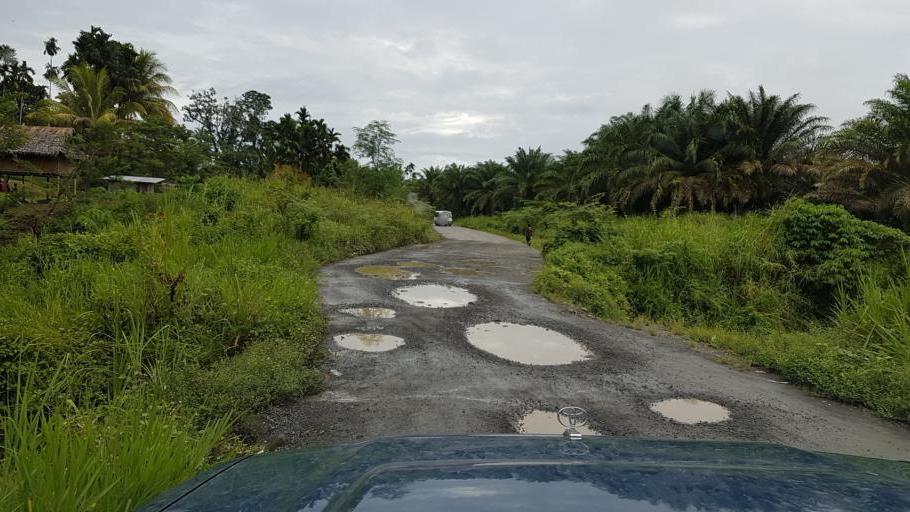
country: PG
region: Northern Province
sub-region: Sohe
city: Popondetta
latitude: -8.8242
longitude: 148.0730
